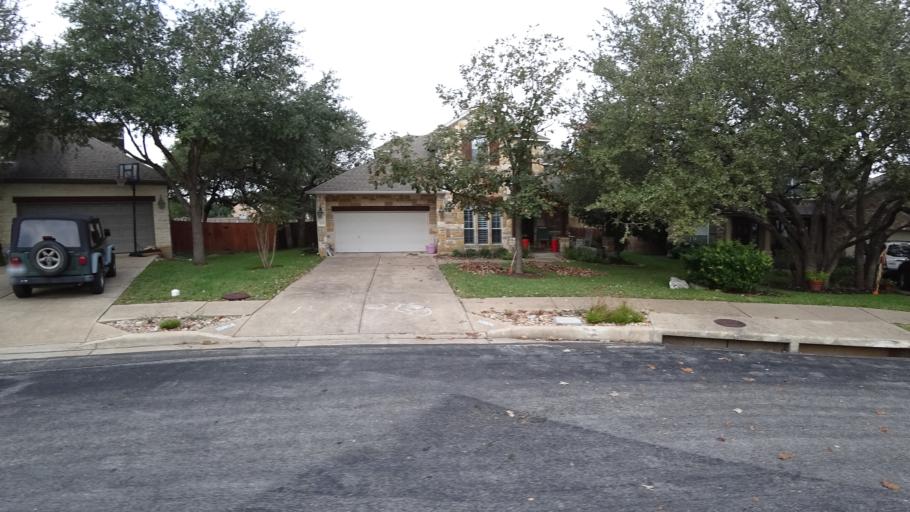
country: US
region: Texas
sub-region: Travis County
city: Shady Hollow
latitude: 30.1923
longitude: -97.8975
